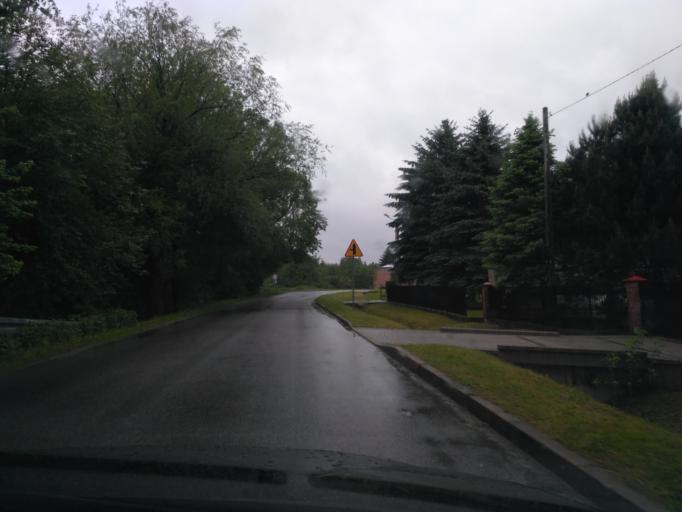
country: PL
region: Lesser Poland Voivodeship
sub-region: Powiat gorlicki
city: Sekowa
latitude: 49.6170
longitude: 21.2063
